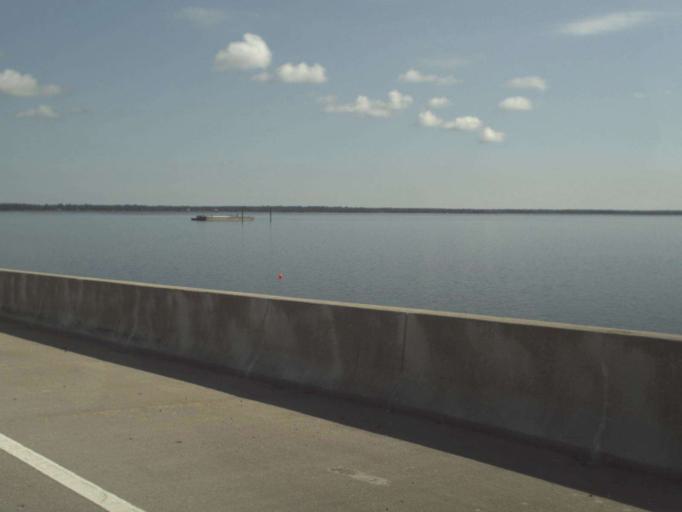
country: US
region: Florida
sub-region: Walton County
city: Seaside
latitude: 30.4044
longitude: -86.1668
